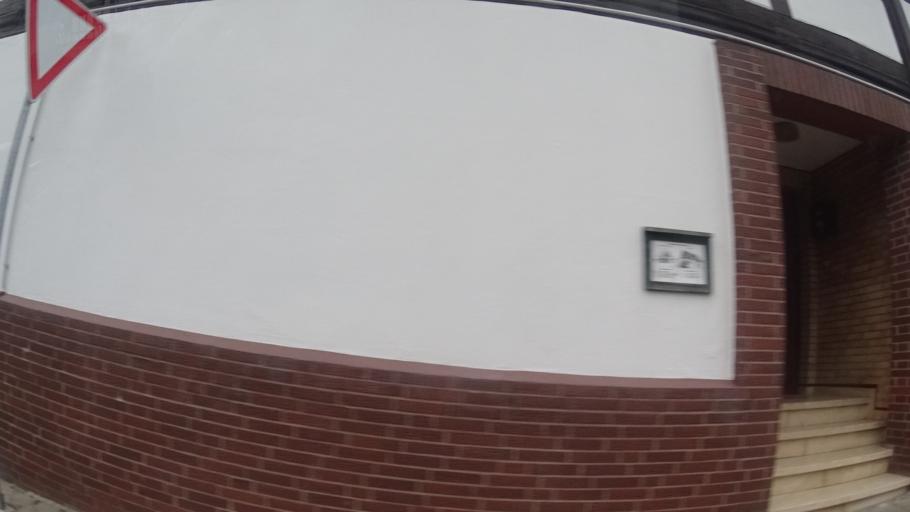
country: DE
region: Lower Saxony
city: Pegestorf
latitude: 51.9280
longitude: 9.5106
